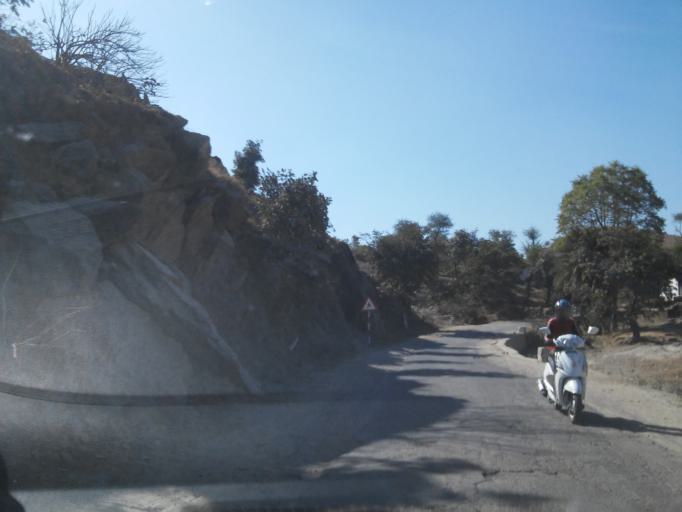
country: IN
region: Rajasthan
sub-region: Udaipur
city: Udaipur
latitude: 24.5002
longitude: 73.6136
